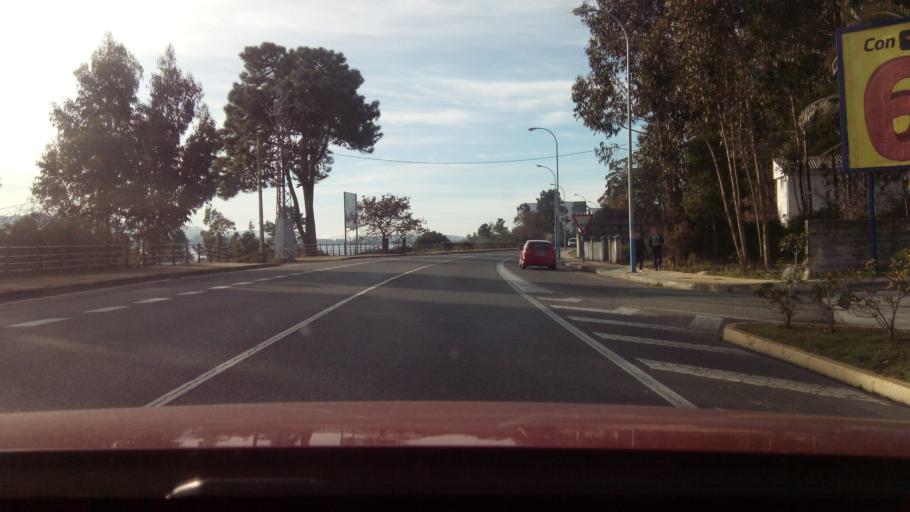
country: ES
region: Galicia
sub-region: Provincia de Pontevedra
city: O Grove
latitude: 42.4721
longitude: -8.8622
